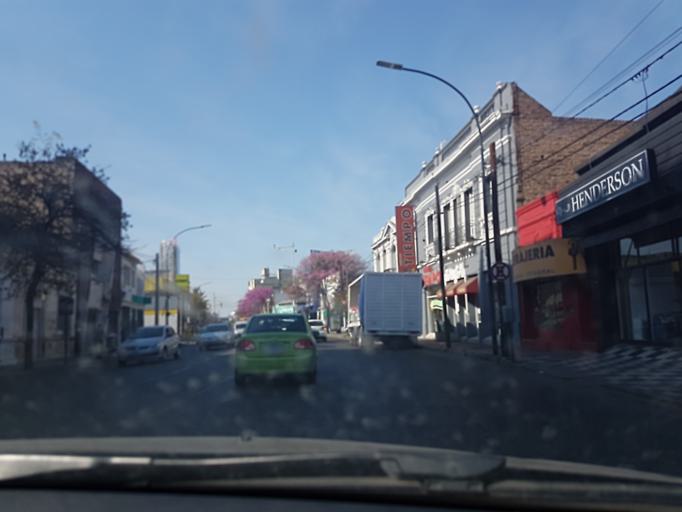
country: AR
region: Cordoba
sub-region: Departamento de Capital
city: Cordoba
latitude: -31.3998
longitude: -64.1976
